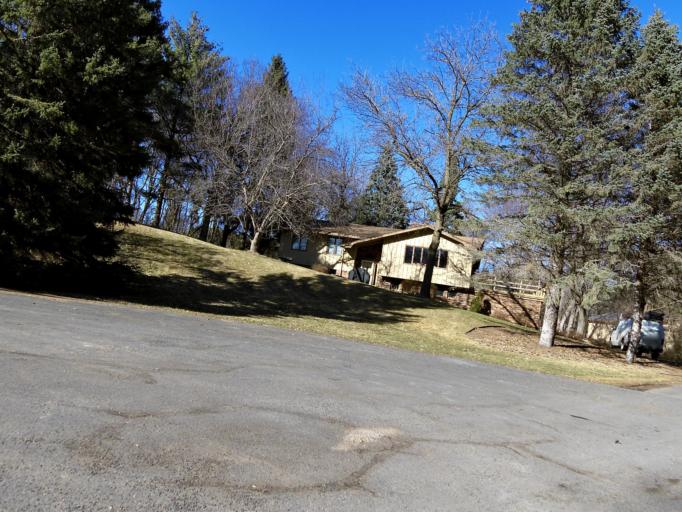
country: US
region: Minnesota
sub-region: Washington County
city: Lake Elmo
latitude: 44.9810
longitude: -92.8247
